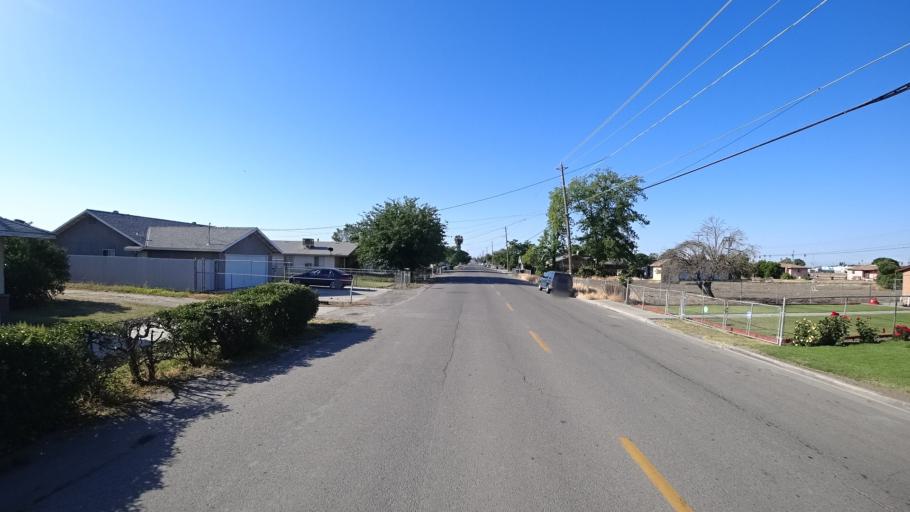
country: US
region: California
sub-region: Kings County
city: Corcoran
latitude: 36.1045
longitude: -119.5543
